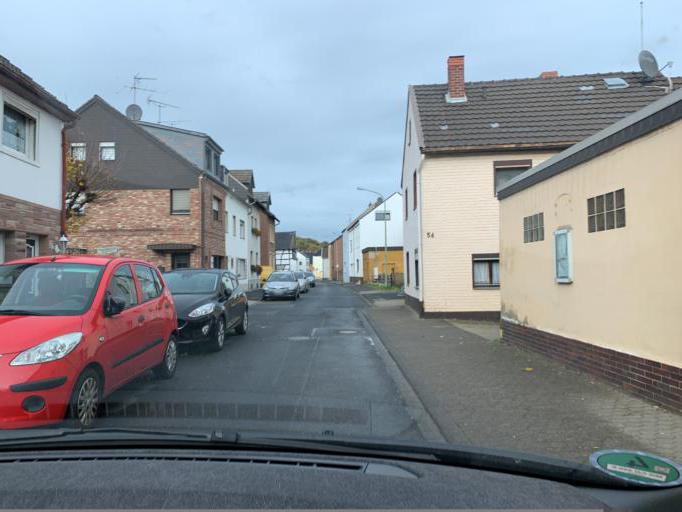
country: DE
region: North Rhine-Westphalia
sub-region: Regierungsbezirk Koln
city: Kreuzau
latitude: 50.7369
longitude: 6.4789
